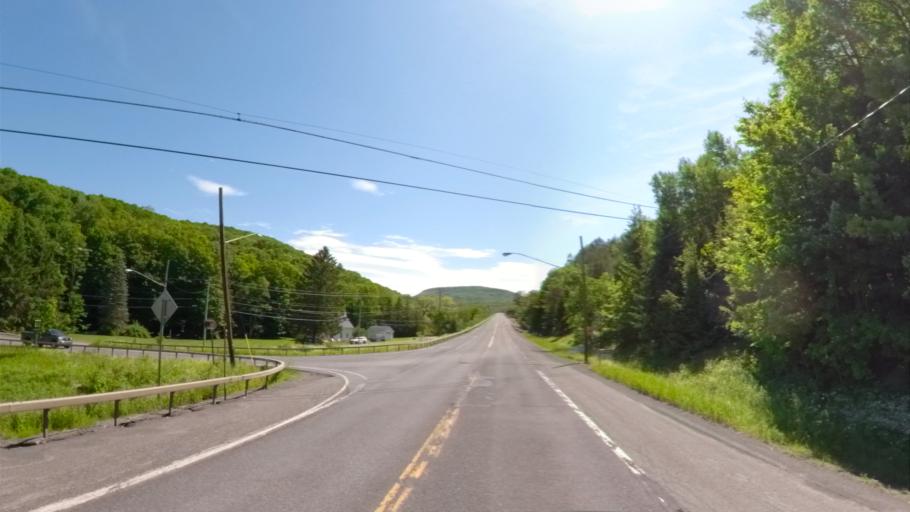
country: US
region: New York
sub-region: Delaware County
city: Stamford
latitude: 42.1505
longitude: -74.5191
